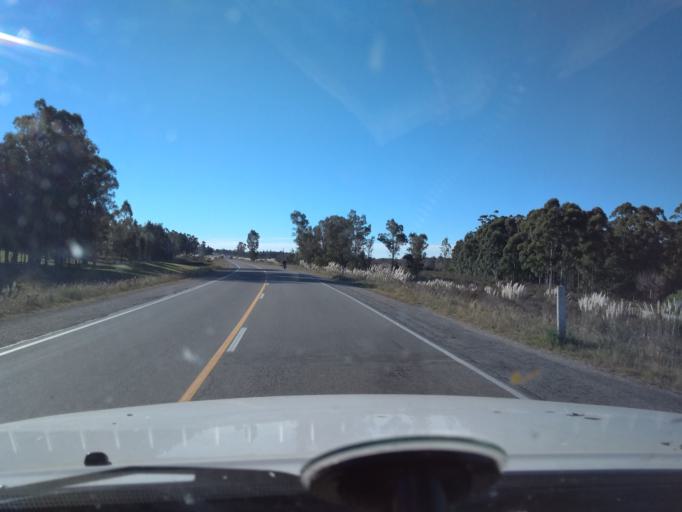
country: UY
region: Canelones
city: Sauce
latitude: -34.6078
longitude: -56.0483
